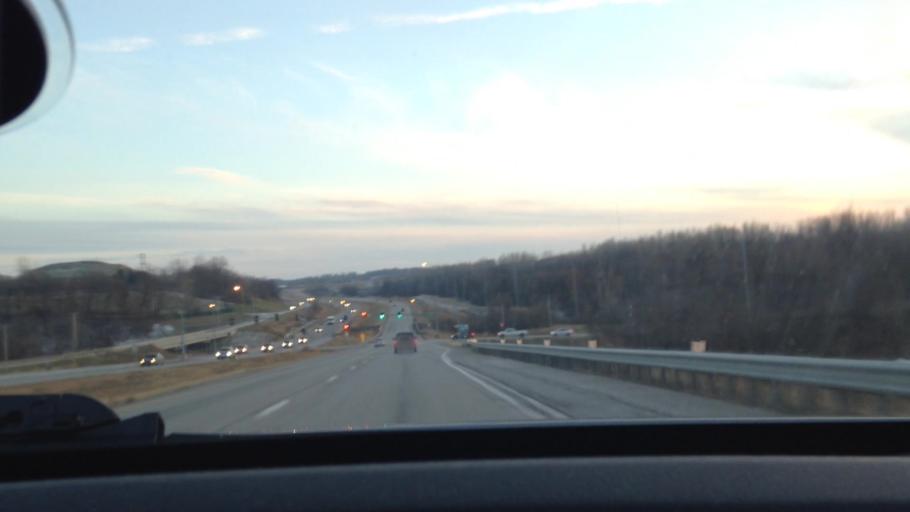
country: US
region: Missouri
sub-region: Jackson County
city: Independence
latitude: 39.1481
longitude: -94.3921
